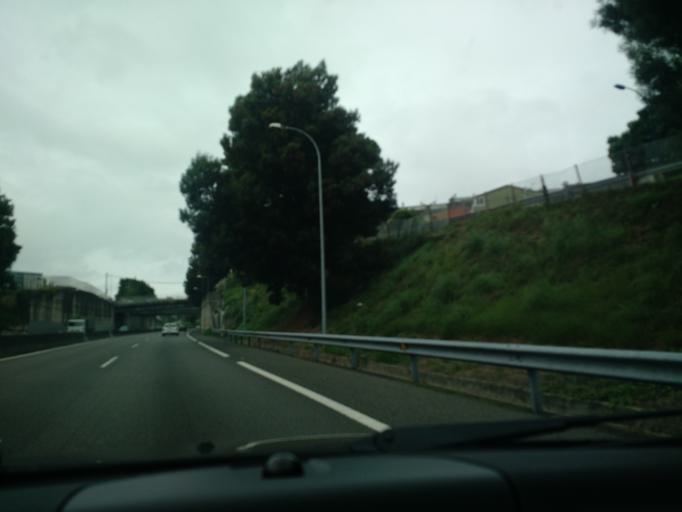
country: ES
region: Galicia
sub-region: Provincia da Coruna
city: Culleredo
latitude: 43.3132
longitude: -8.3809
